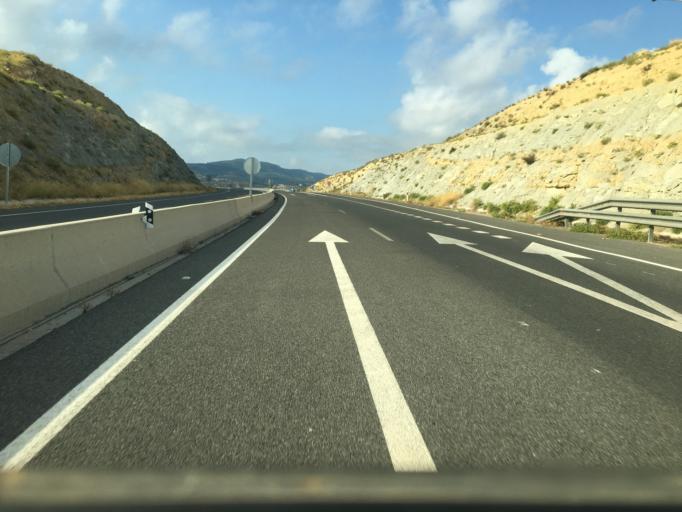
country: ES
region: Murcia
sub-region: Murcia
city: Beniel
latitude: 37.9832
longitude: -0.9746
